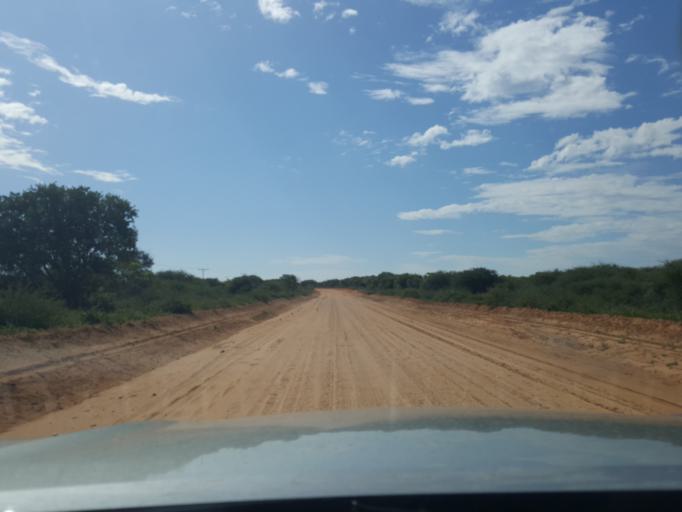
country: BW
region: Kweneng
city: Khudumelapye
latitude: -23.8094
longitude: 24.8181
